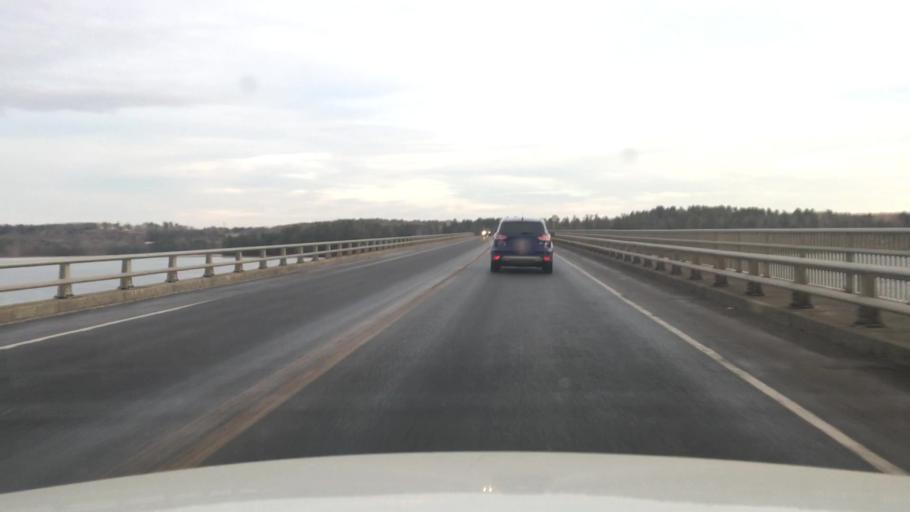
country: US
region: Maine
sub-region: Lincoln County
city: Wiscasset
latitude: 44.0018
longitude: -69.6622
